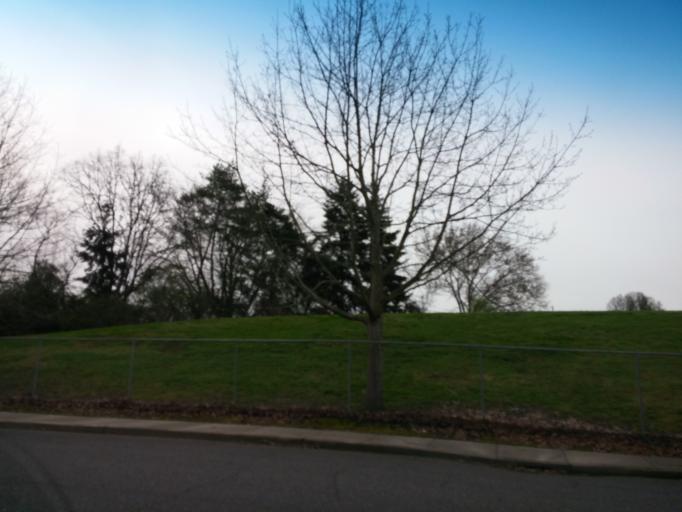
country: US
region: Oregon
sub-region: Washington County
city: Cedar Mill
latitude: 45.5090
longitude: -122.8160
